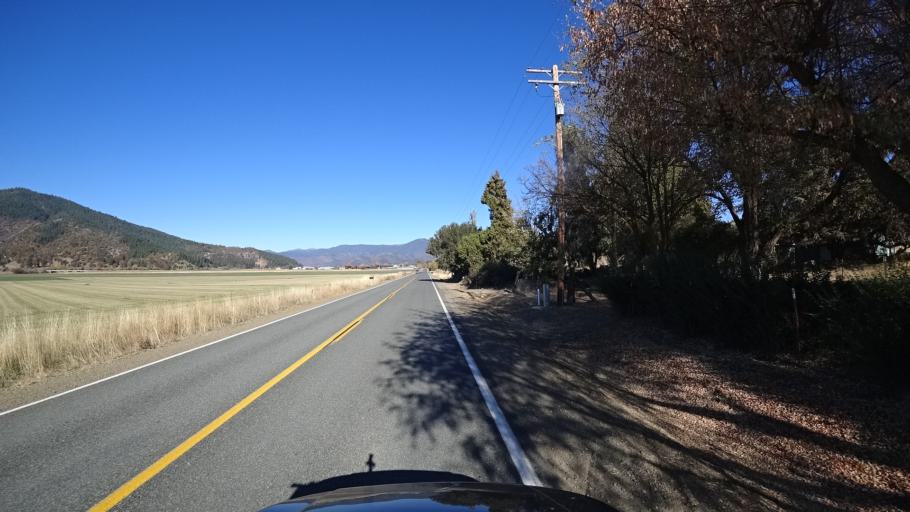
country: US
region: California
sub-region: Siskiyou County
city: Yreka
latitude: 41.5946
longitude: -122.8411
